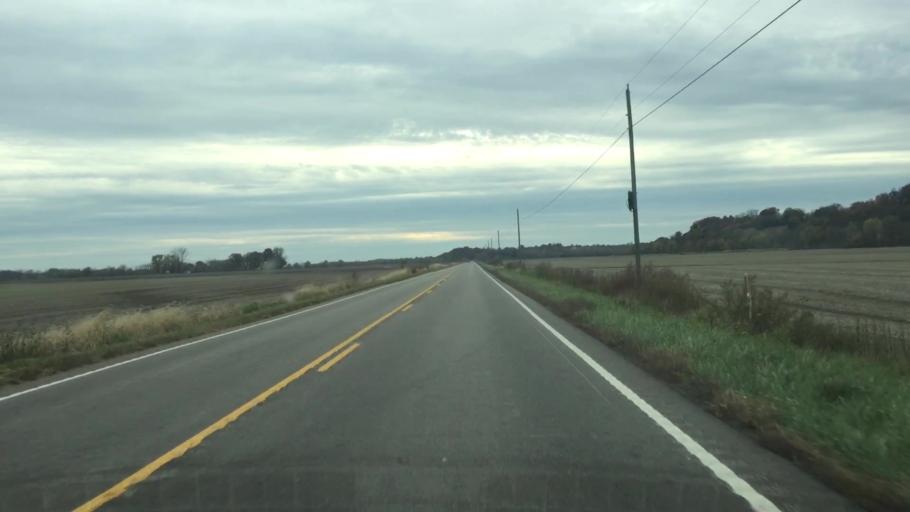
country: US
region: Missouri
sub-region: Callaway County
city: Fulton
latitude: 38.7063
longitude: -91.7968
